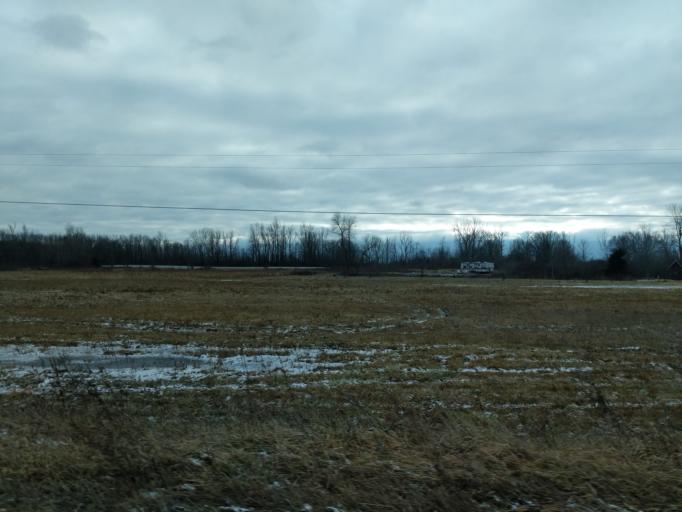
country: US
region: Michigan
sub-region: Lapeer County
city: North Branch
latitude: 43.3245
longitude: -83.2543
